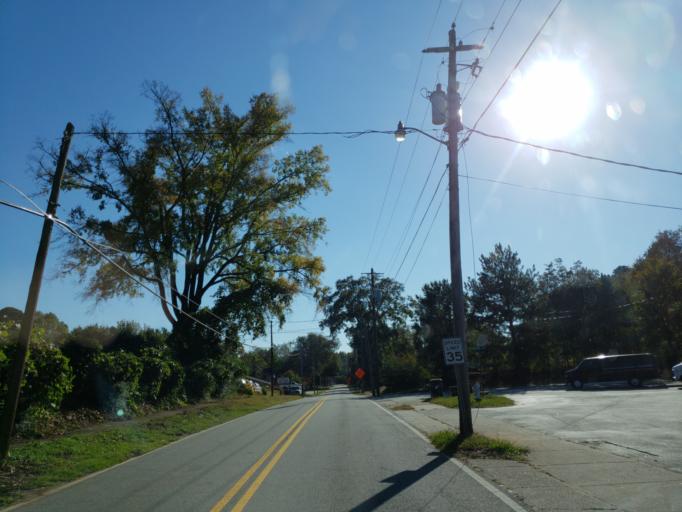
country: US
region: Georgia
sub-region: Gwinnett County
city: Lawrenceville
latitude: 33.9662
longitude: -83.9871
